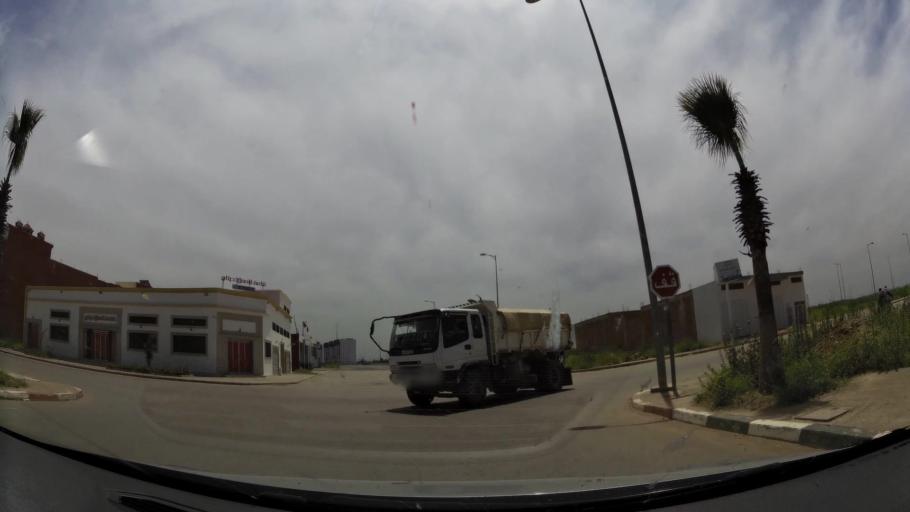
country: MA
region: Rabat-Sale-Zemmour-Zaer
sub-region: Khemisset
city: Khemisset
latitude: 33.8211
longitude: -6.0854
